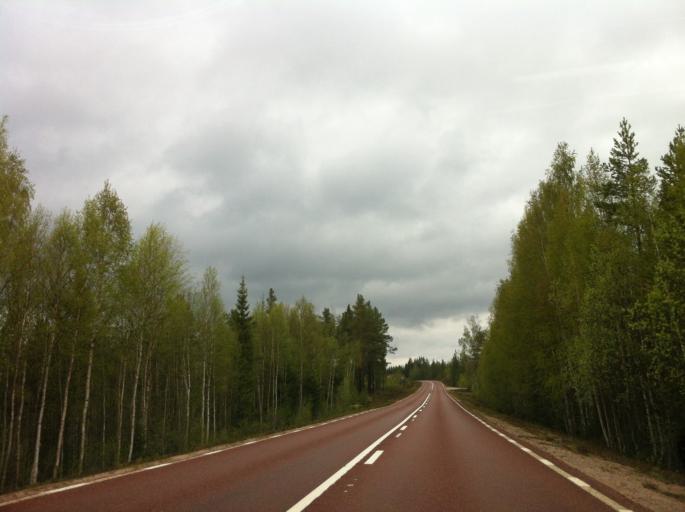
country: SE
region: Jaemtland
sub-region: Harjedalens Kommun
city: Sveg
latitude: 61.9048
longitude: 14.6213
